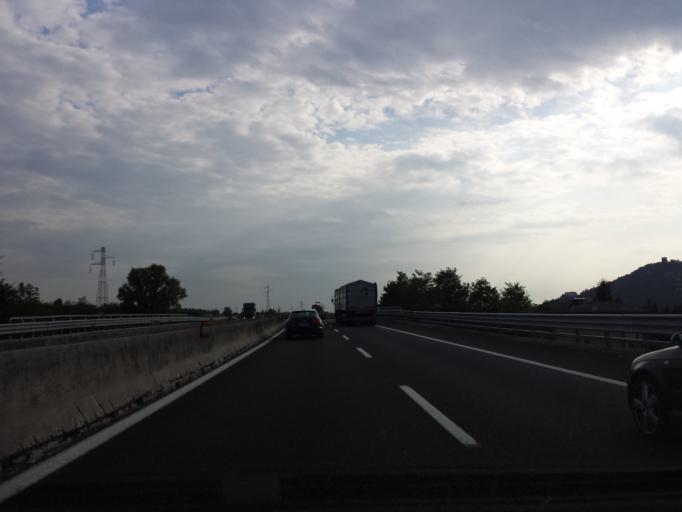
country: IT
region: Veneto
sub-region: Provincia di Padova
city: Pernumia
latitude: 45.2550
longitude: 11.7756
